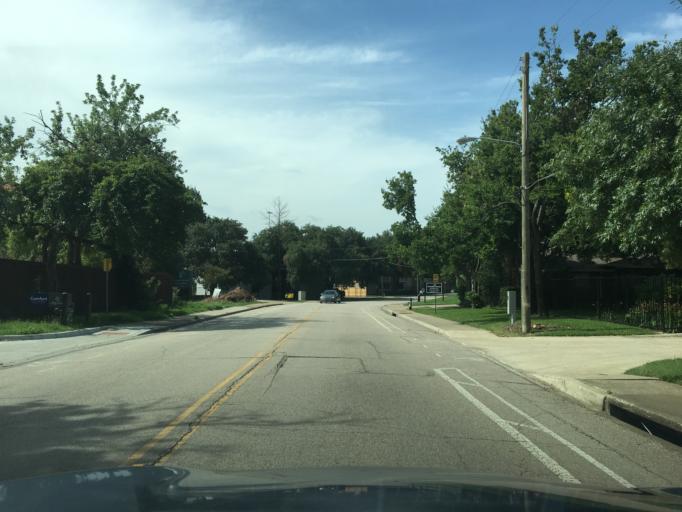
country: US
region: Texas
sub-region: Dallas County
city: Richardson
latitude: 32.9300
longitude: -96.7645
